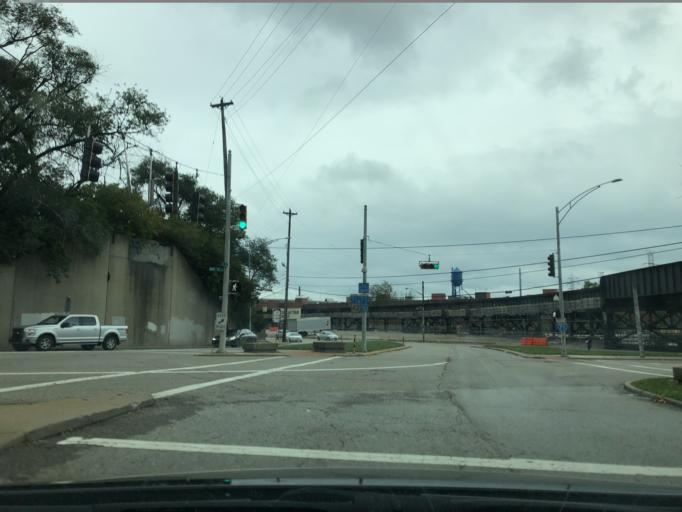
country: US
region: Kentucky
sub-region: Kenton County
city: Ludlow
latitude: 39.0977
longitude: -84.5264
